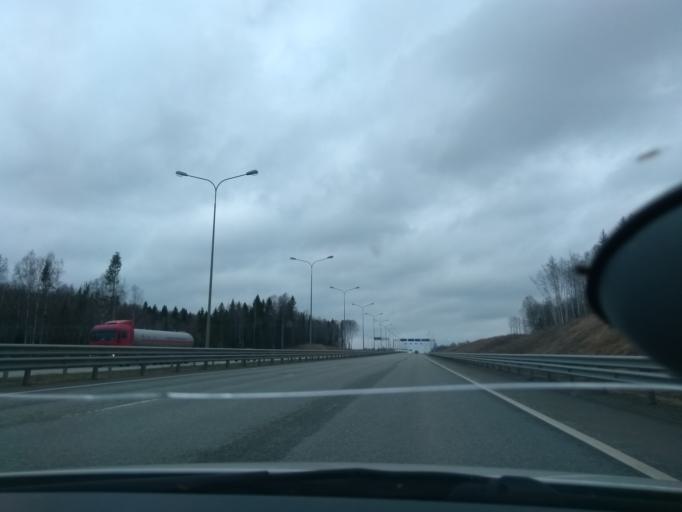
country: RU
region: Perm
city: Bershet'
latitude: 57.7302
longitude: 56.3480
